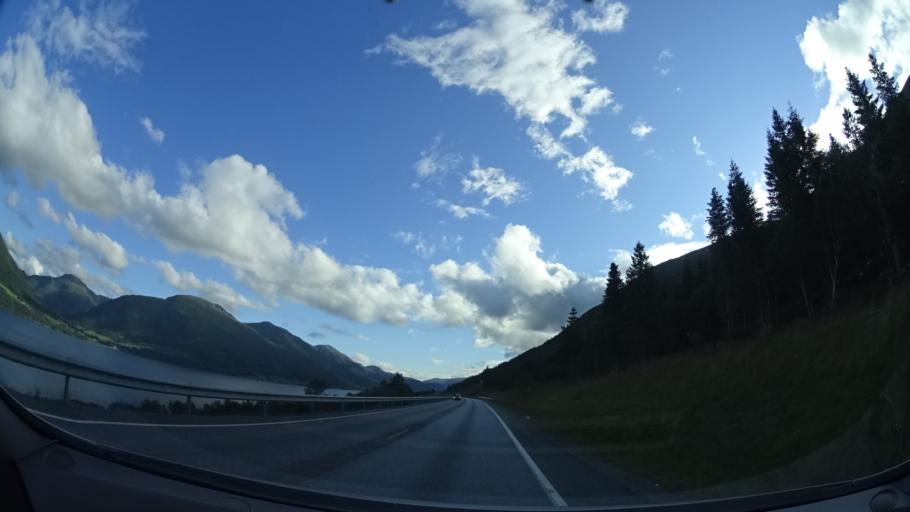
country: NO
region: More og Romsdal
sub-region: Gjemnes
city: Batnfjordsora
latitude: 62.9439
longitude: 7.7440
